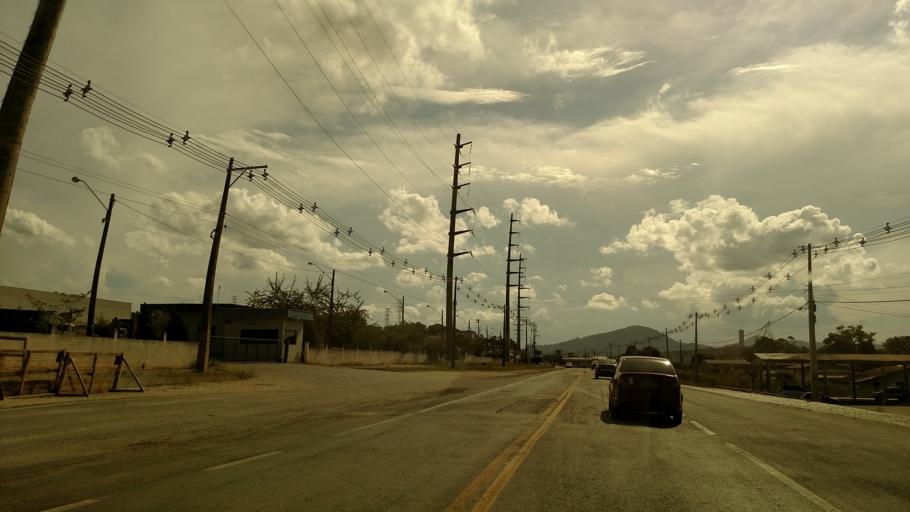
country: BR
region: Santa Catarina
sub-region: Itajai
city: Itajai
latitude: -26.9459
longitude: -48.7292
